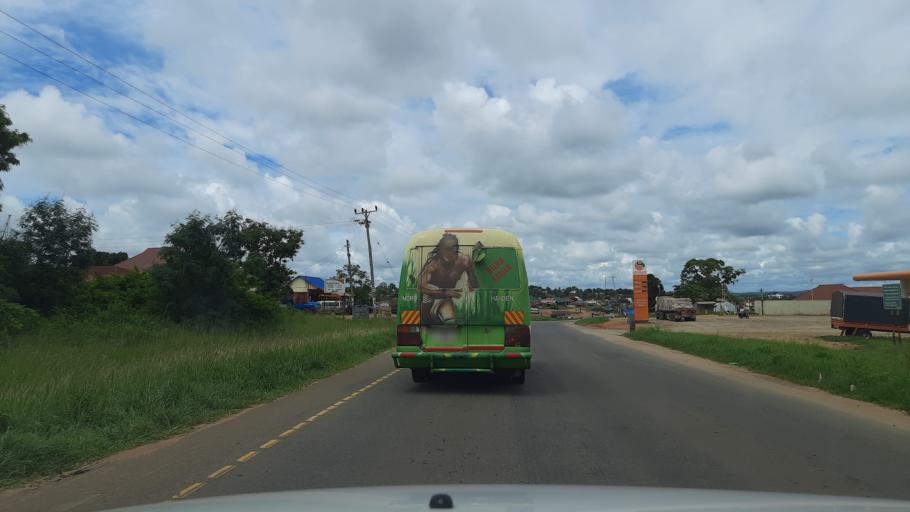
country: TZ
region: Tanga
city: Chanika
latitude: -5.7907
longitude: 38.2899
